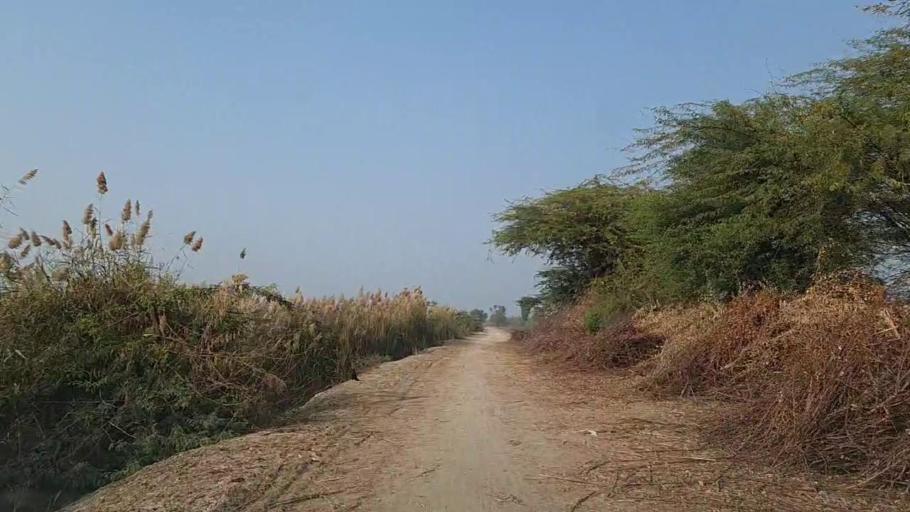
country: PK
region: Sindh
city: Nawabshah
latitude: 26.3502
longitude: 68.4740
